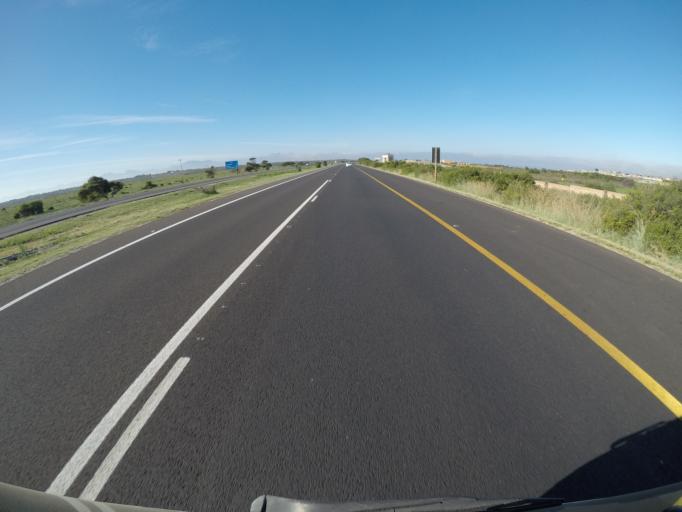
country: ZA
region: Western Cape
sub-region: Eden District Municipality
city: Mossel Bay
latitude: -34.1764
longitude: 22.0656
